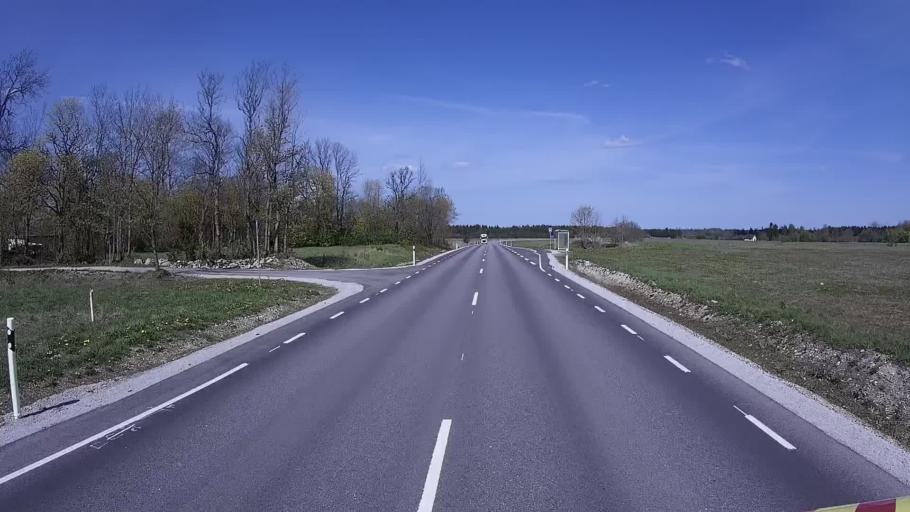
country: EE
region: Harju
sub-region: Paldiski linn
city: Paldiski
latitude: 59.2096
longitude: 24.0949
